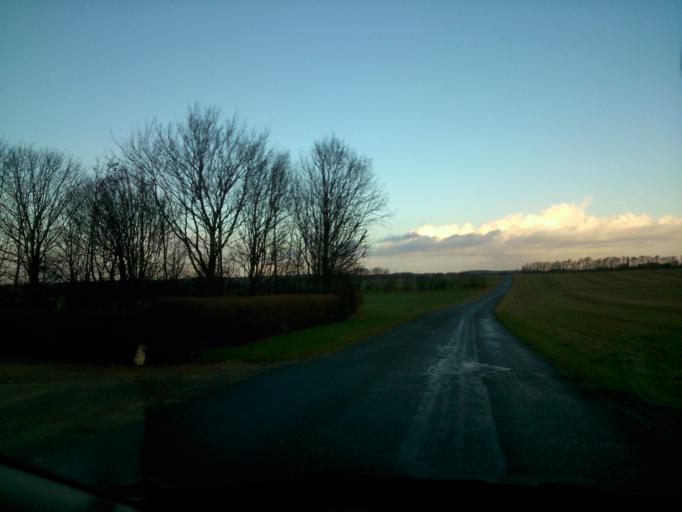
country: DK
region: Central Jutland
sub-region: Ringkobing-Skjern Kommune
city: Videbaek
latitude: 56.0517
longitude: 8.5766
